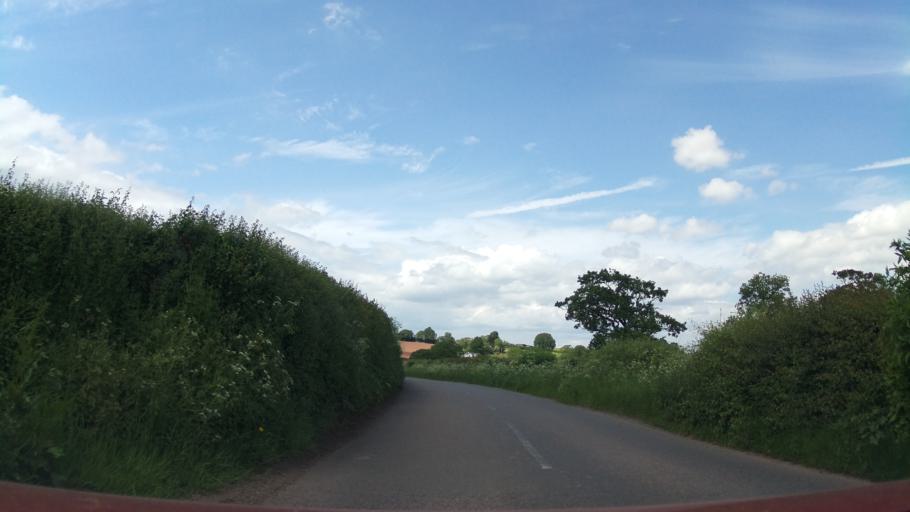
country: GB
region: England
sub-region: Herefordshire
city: Llanrothal
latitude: 51.8364
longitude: -2.7632
